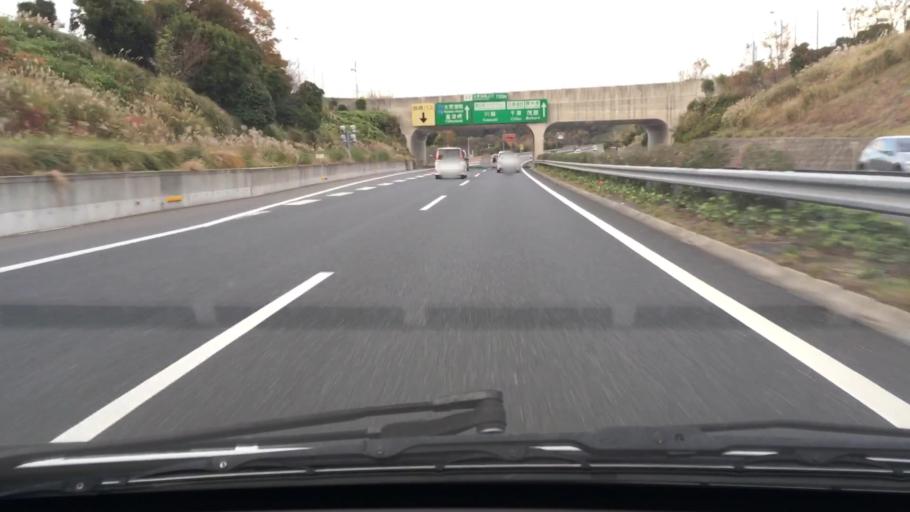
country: JP
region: Chiba
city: Kisarazu
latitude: 35.3451
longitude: 139.9444
